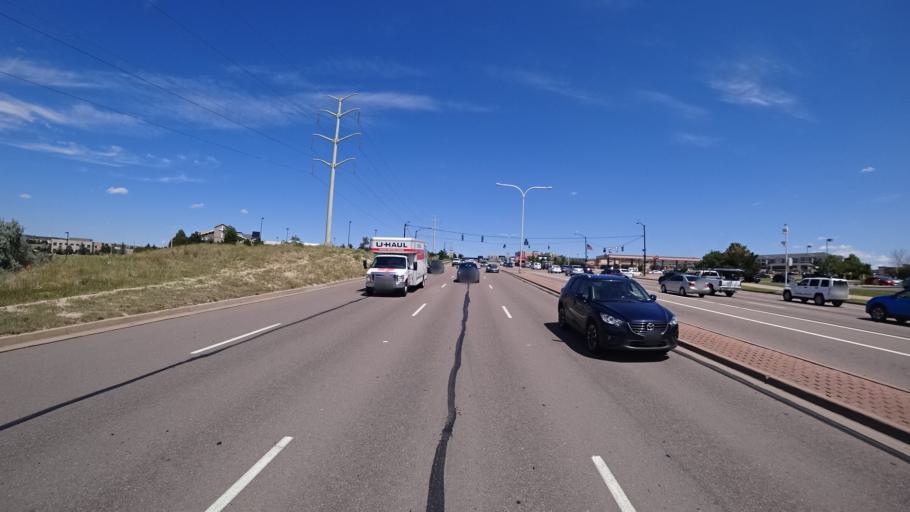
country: US
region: Colorado
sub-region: El Paso County
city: Black Forest
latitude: 38.9403
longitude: -104.7302
